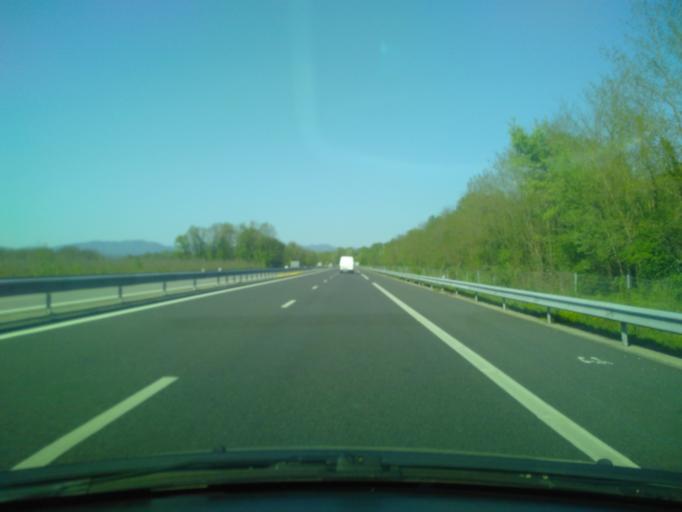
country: FR
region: Rhone-Alpes
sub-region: Departement de l'Isere
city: Saint-Quentin-sur-Isere
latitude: 45.2596
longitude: 5.5132
